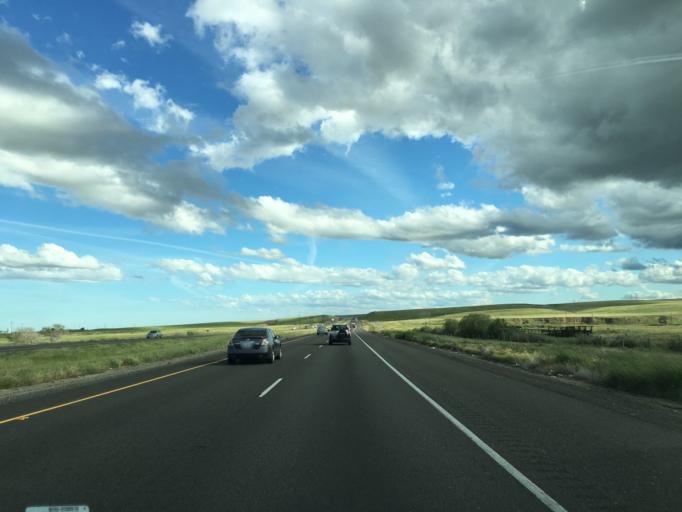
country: US
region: California
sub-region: Merced County
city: Los Banos
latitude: 37.0022
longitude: -120.9173
